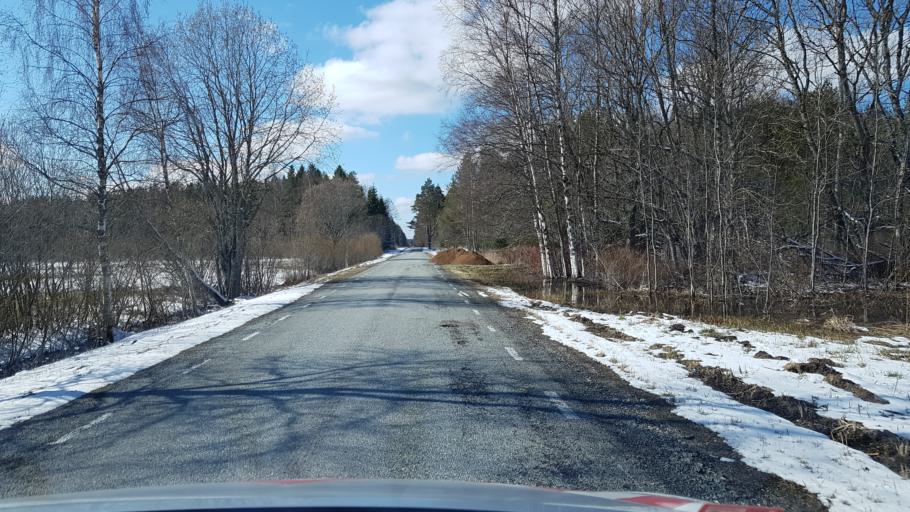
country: EE
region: Laeaene-Virumaa
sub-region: Kadrina vald
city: Kadrina
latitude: 59.5296
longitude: 26.0237
